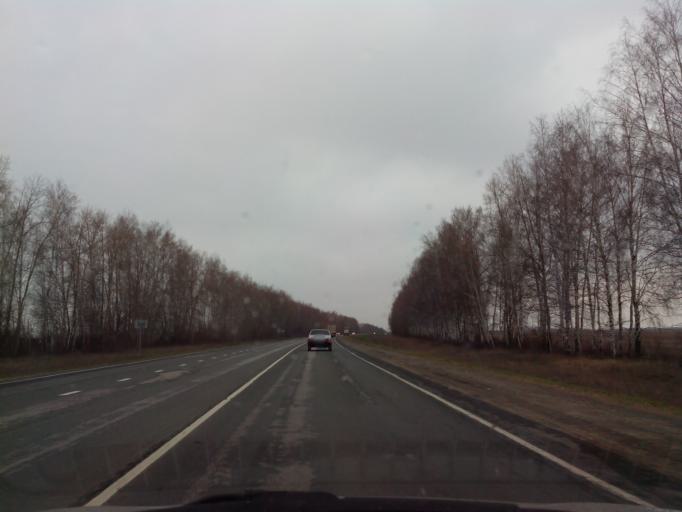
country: RU
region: Tambov
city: Pervomayskiy
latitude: 53.0941
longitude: 40.3969
